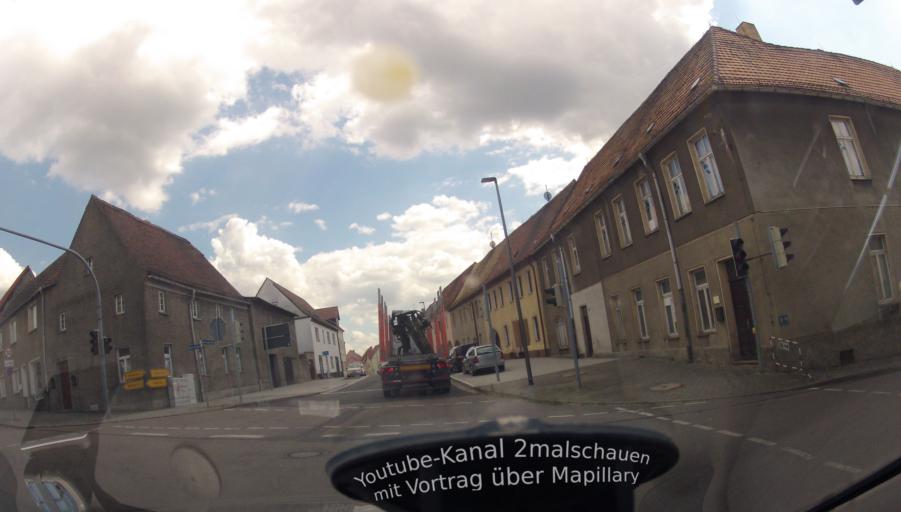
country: DE
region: Saxony
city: Schildau
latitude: 51.4566
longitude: 12.9273
